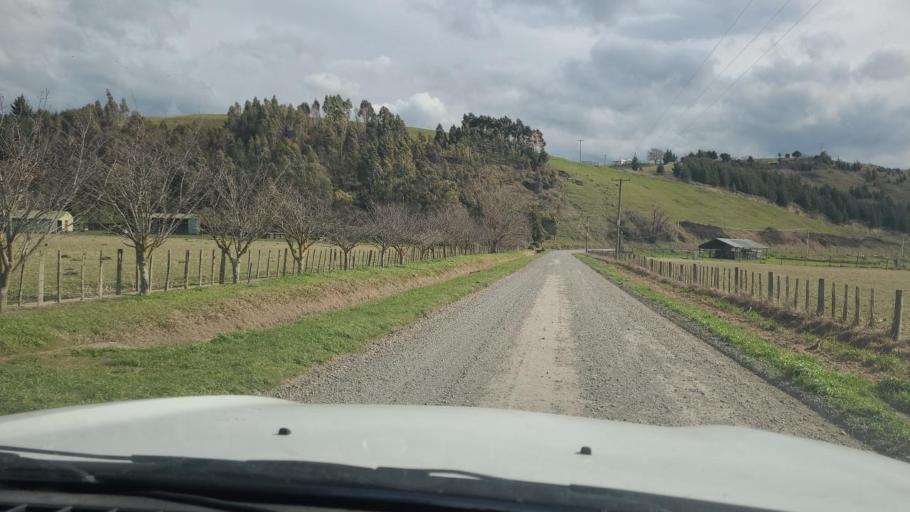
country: NZ
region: Hawke's Bay
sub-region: Napier City
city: Taradale
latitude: -39.5634
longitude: 176.7626
